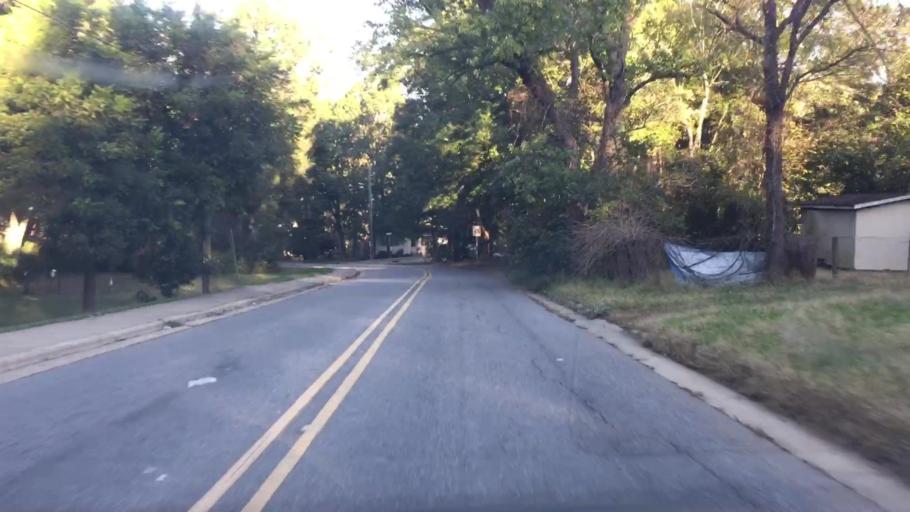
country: US
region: North Carolina
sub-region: Iredell County
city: Mooresville
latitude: 35.5747
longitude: -80.8139
